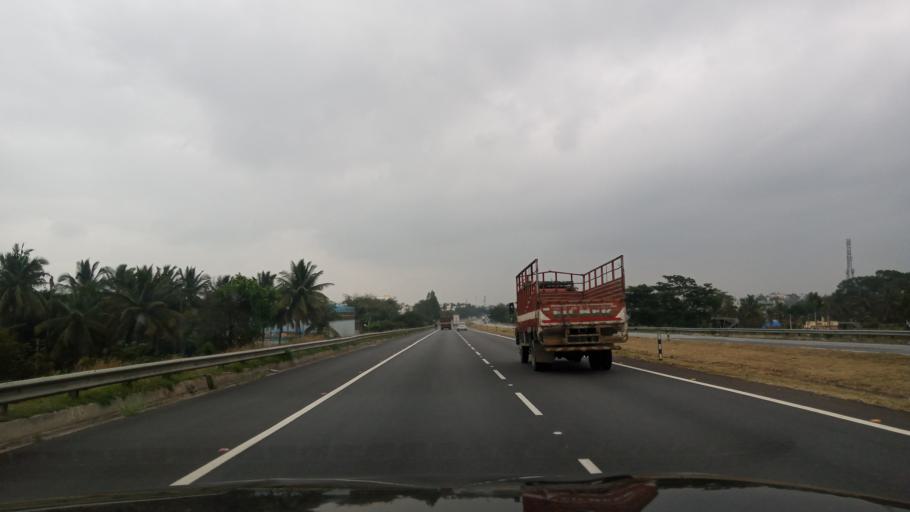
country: IN
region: Karnataka
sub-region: Bangalore Urban
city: Bangalore
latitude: 13.0026
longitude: 77.4743
